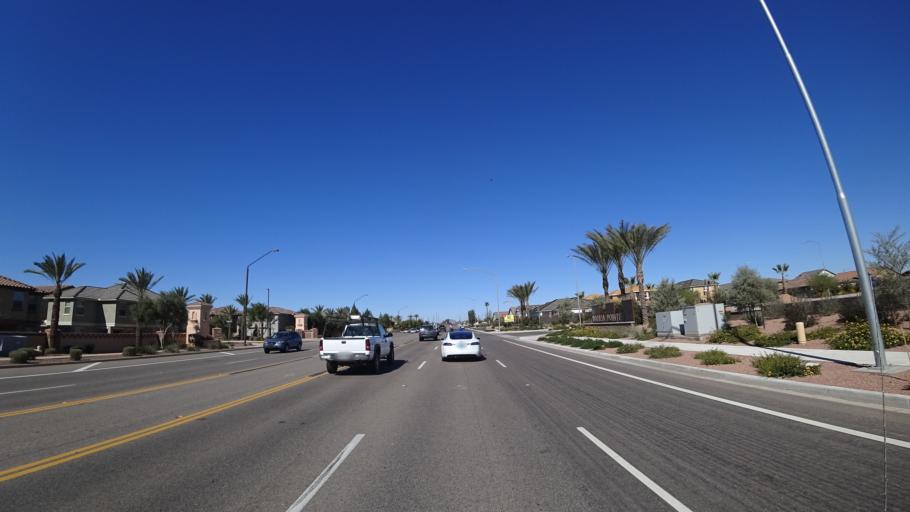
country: US
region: Arizona
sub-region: Maricopa County
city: Gilbert
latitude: 33.3582
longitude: -111.6875
